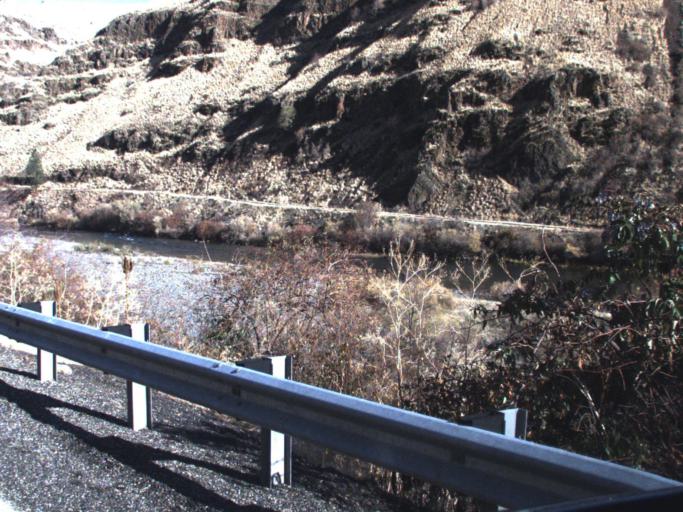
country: US
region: Washington
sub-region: Asotin County
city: Asotin
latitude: 46.0379
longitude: -117.2549
